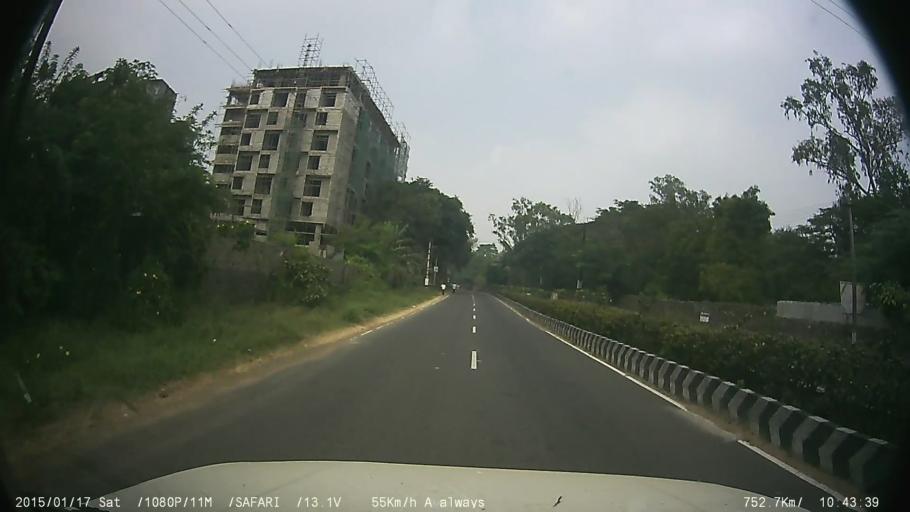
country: IN
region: Tamil Nadu
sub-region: Kancheepuram
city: Vandalur
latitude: 12.8762
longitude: 80.0871
